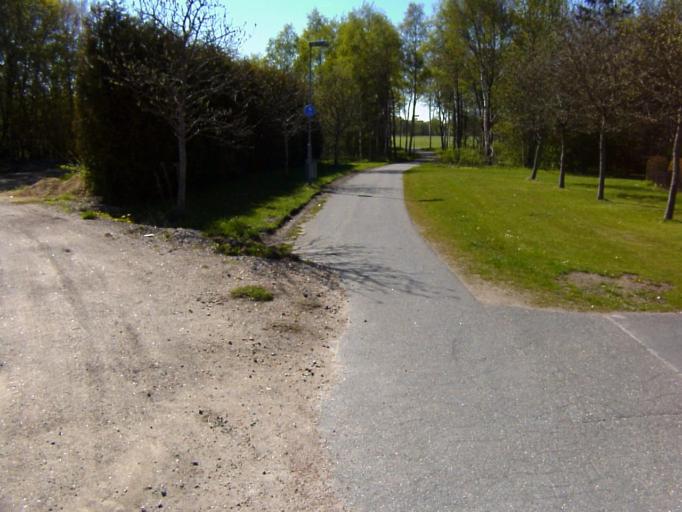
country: SE
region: Skane
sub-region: Kristianstads Kommun
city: Kristianstad
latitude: 56.0309
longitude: 14.1928
